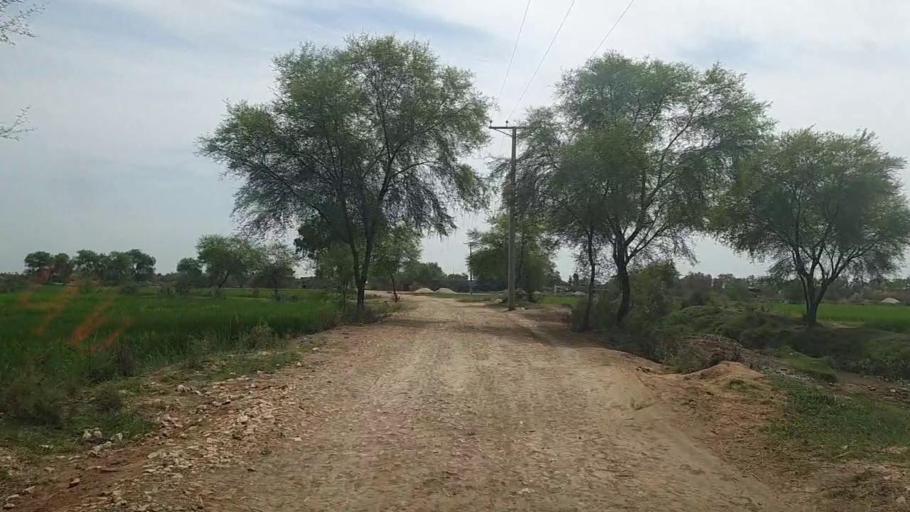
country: PK
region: Sindh
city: Thul
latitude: 28.2535
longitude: 68.6984
